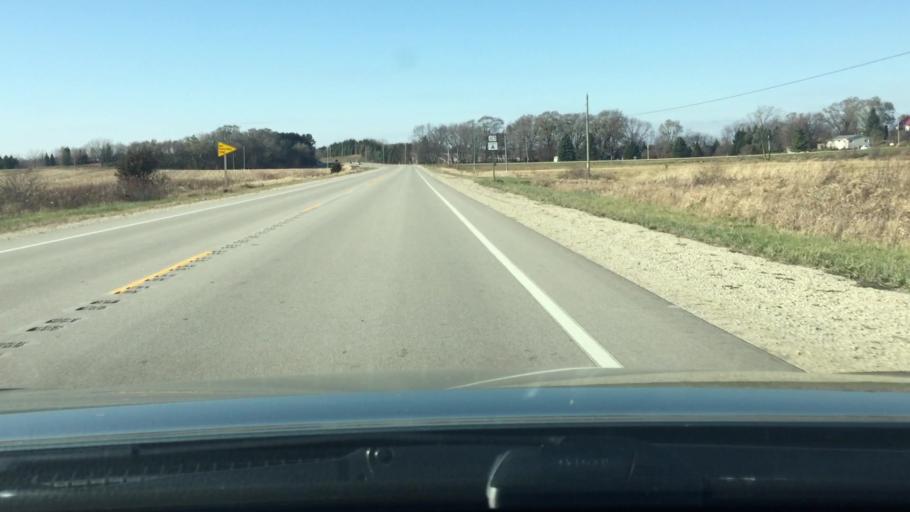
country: US
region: Wisconsin
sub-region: Jefferson County
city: Lake Ripley
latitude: 43.0109
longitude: -88.9605
